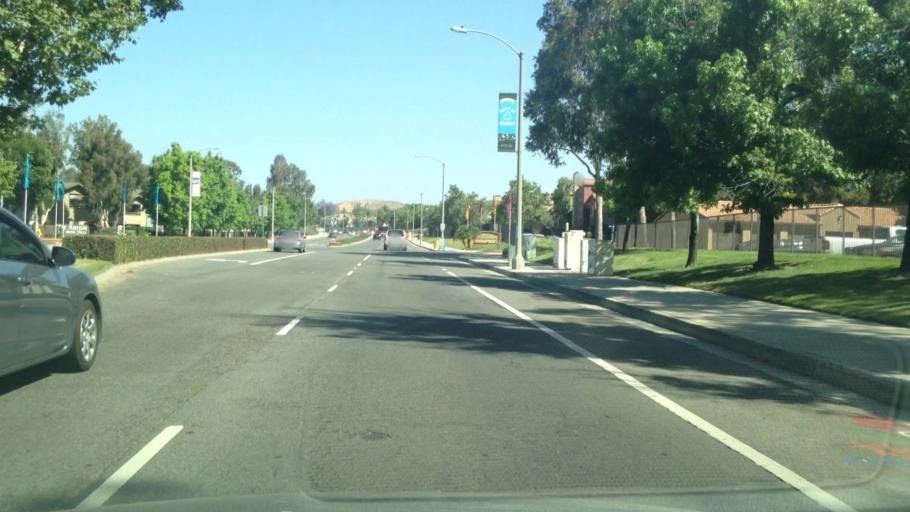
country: US
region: California
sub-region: Riverside County
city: Home Gardens
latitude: 33.8922
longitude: -117.5226
